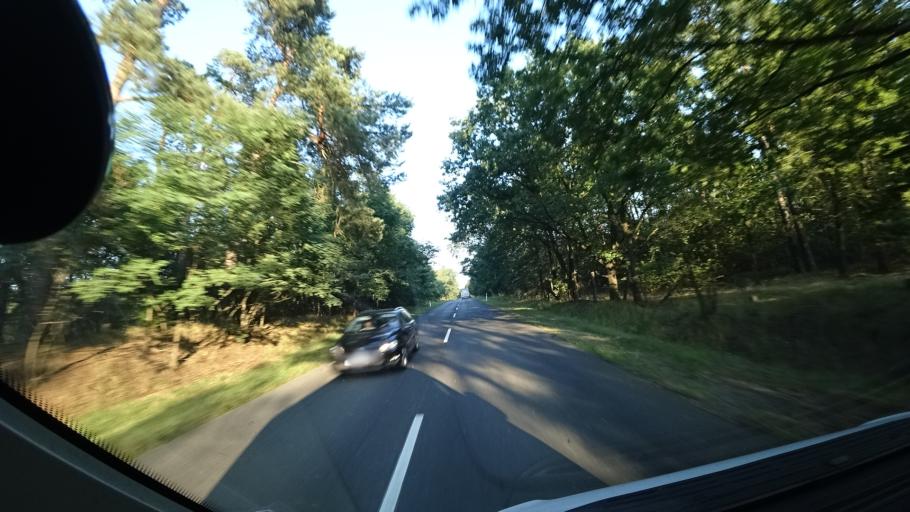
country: PL
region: Opole Voivodeship
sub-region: Powiat kedzierzynsko-kozielski
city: Dziergowice
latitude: 50.2809
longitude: 18.3354
